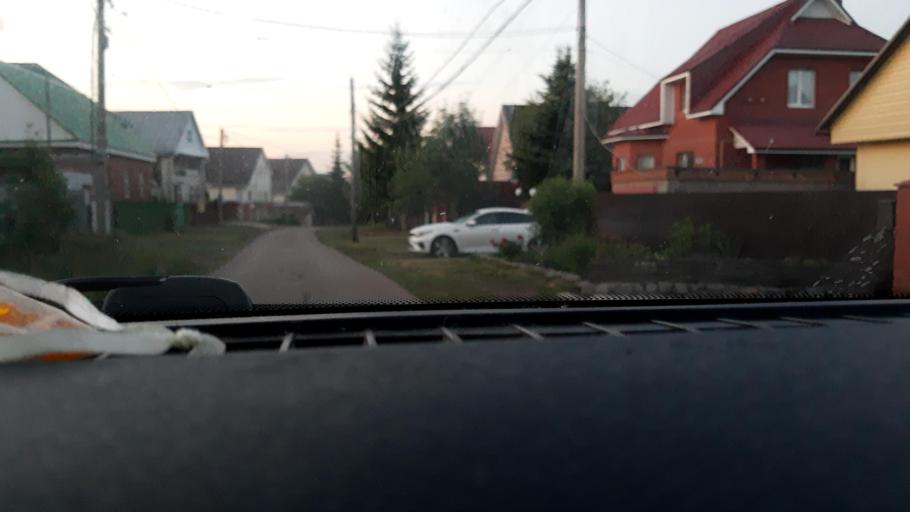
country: RU
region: Bashkortostan
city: Avdon
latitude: 54.6202
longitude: 55.6410
